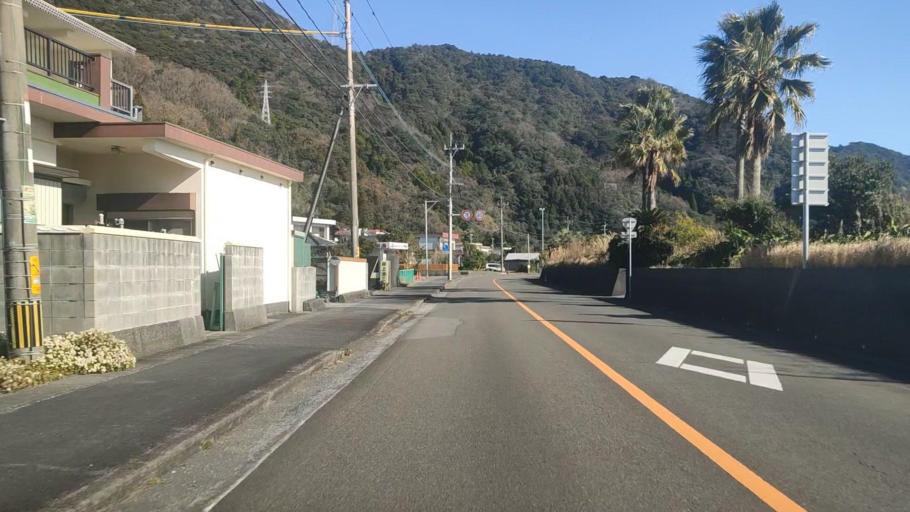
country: JP
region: Oita
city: Saiki
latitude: 32.8079
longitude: 131.9493
